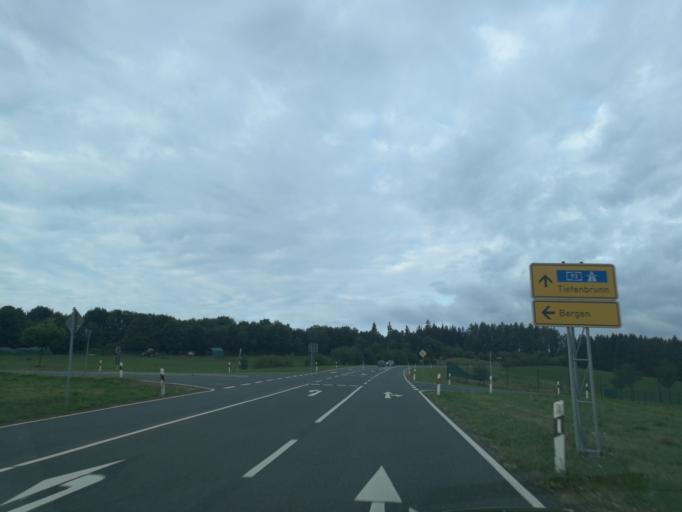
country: DE
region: Saxony
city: Eichigt
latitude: 50.3379
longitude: 12.1829
